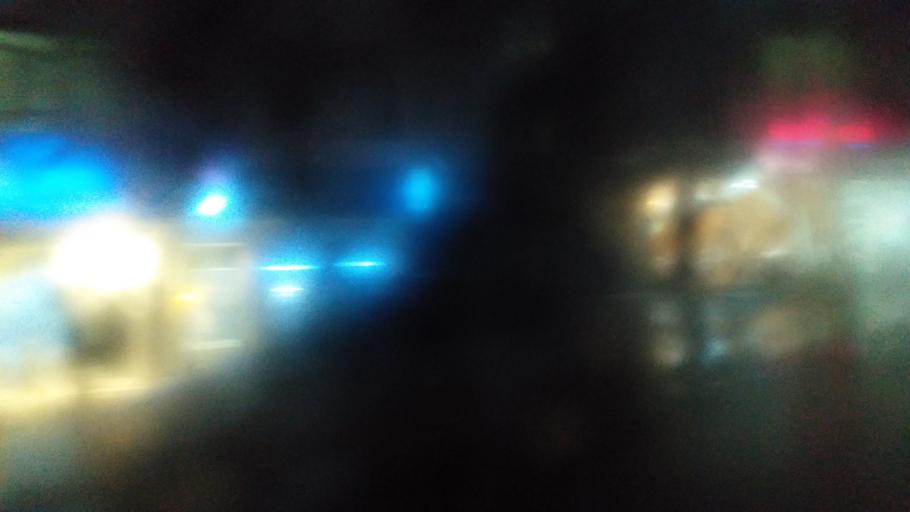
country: TR
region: Ankara
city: Ankara
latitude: 39.9745
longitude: 32.8415
